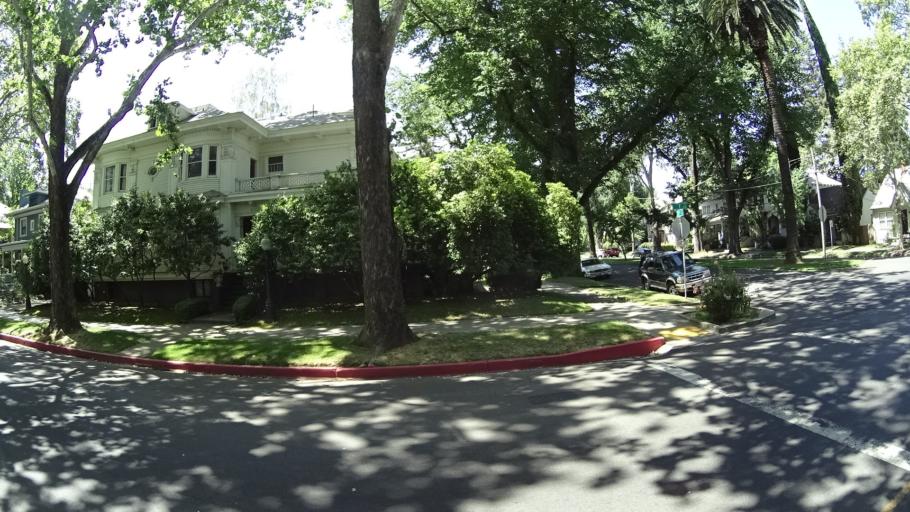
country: US
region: California
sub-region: Sacramento County
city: Sacramento
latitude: 38.5806
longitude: -121.4764
